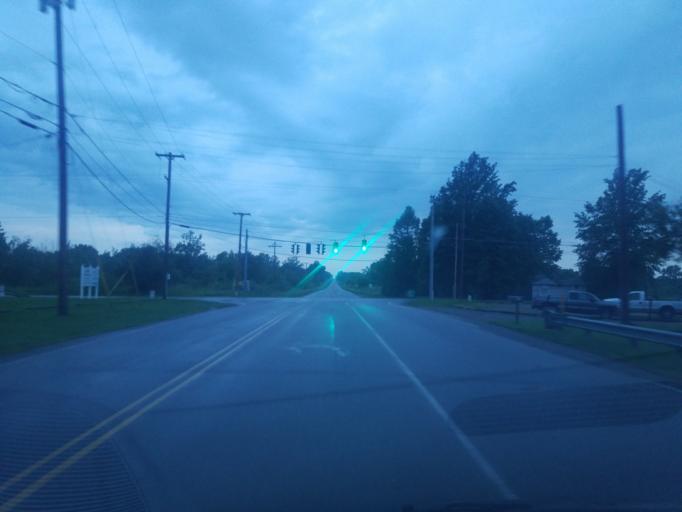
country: US
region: Ohio
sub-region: Mahoning County
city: Canfield
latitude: 40.9882
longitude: -80.7585
